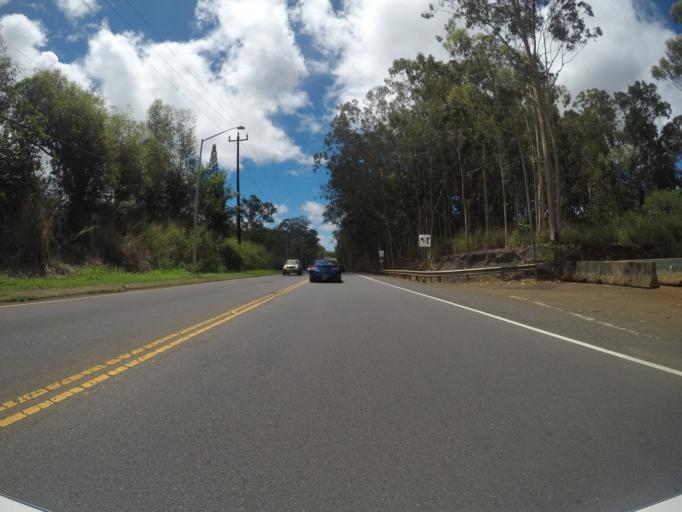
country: US
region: Hawaii
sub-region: Honolulu County
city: Schofield Barracks
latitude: 21.4977
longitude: -158.0512
